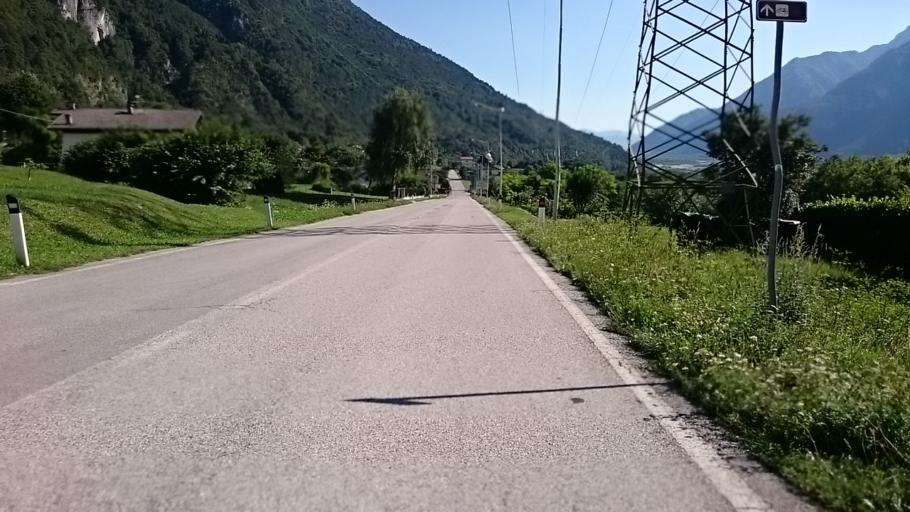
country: IT
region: Veneto
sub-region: Provincia di Belluno
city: Longarone
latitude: 46.2478
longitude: 12.3129
